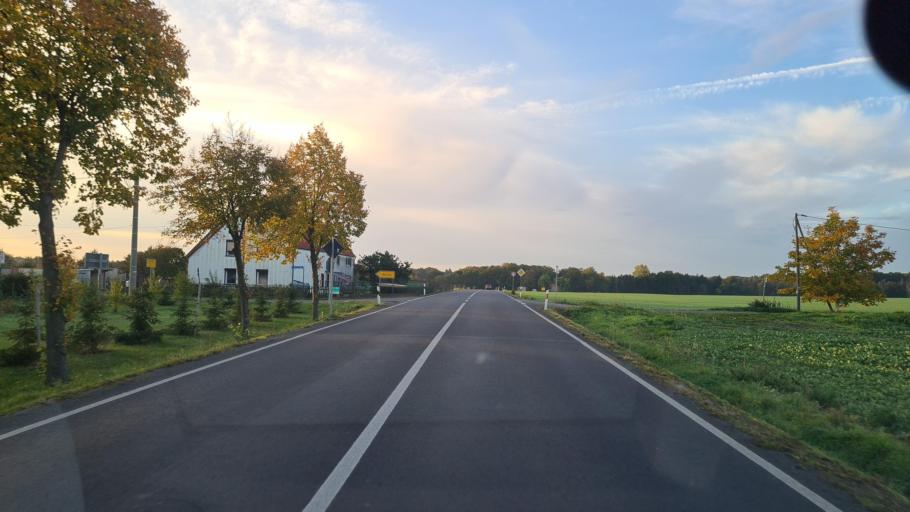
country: DE
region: Saxony
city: Machern
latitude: 51.3895
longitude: 12.6509
